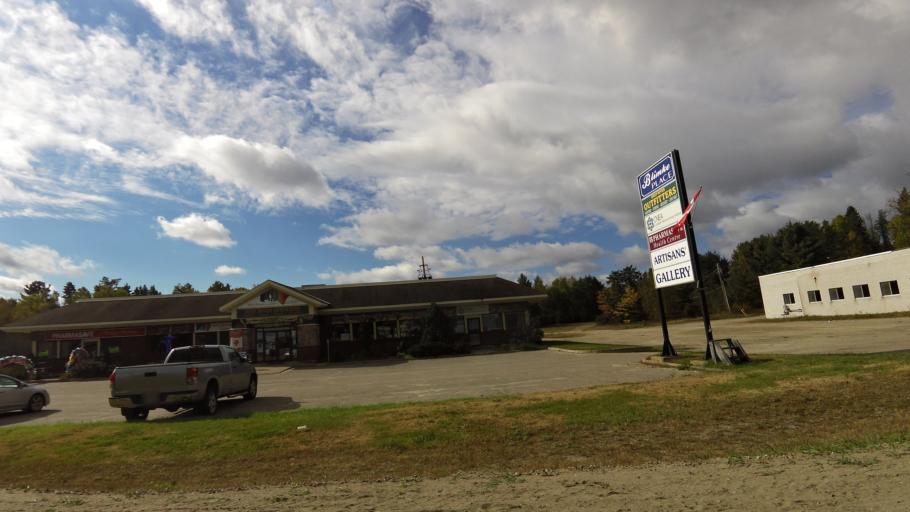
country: CA
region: Ontario
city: Deep River
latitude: 46.1029
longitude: -77.5053
